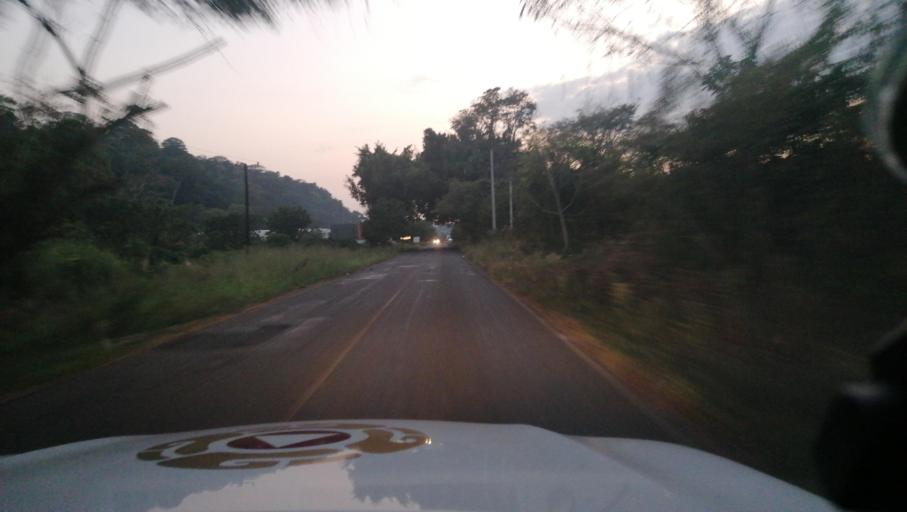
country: MX
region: Chiapas
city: Veinte de Noviembre
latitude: 14.9815
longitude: -92.2440
